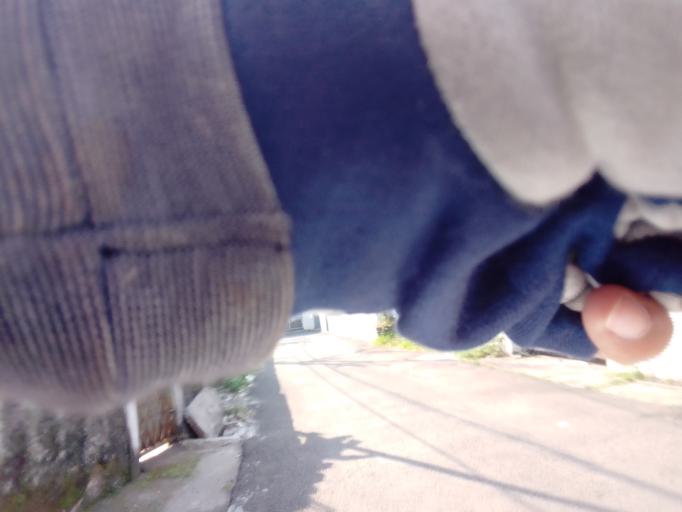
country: ID
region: Jakarta Raya
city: Jakarta
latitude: -6.2639
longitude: 106.8068
